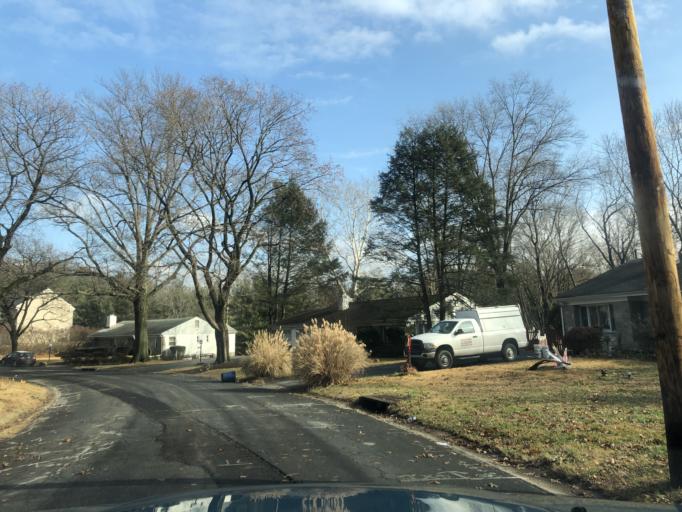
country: US
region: Pennsylvania
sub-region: Delaware County
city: Broomall
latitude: 39.9833
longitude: -75.3405
